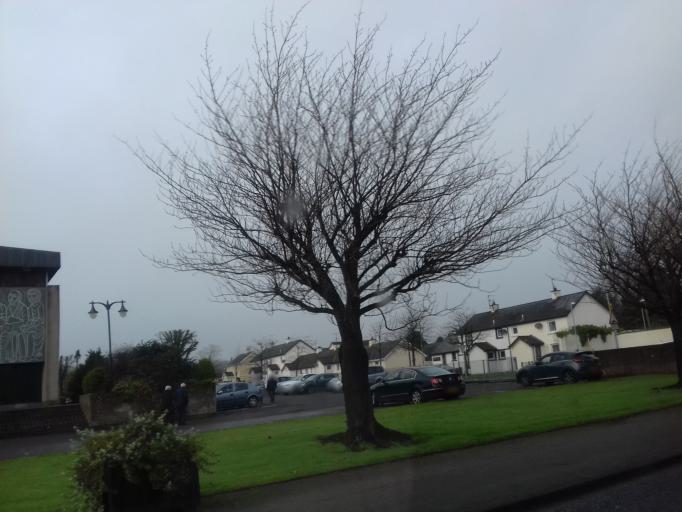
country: GB
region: Northern Ireland
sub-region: Strabane District
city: Sion Mills
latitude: 54.7870
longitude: -7.4727
